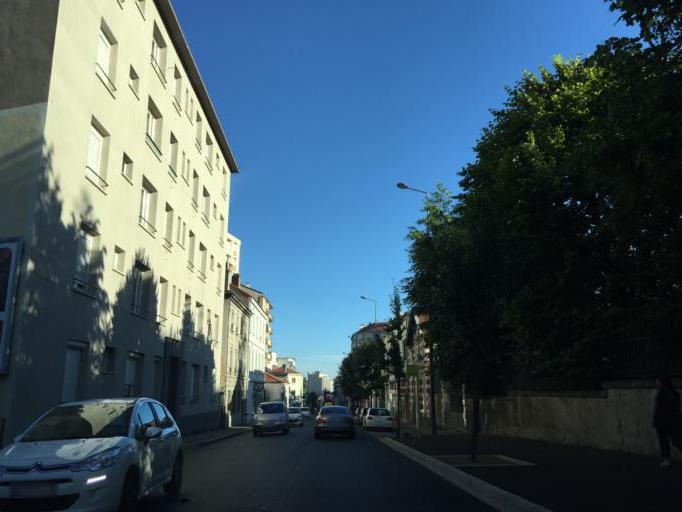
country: FR
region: Rhone-Alpes
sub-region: Departement de la Loire
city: Saint-Etienne
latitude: 45.4126
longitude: 4.3969
